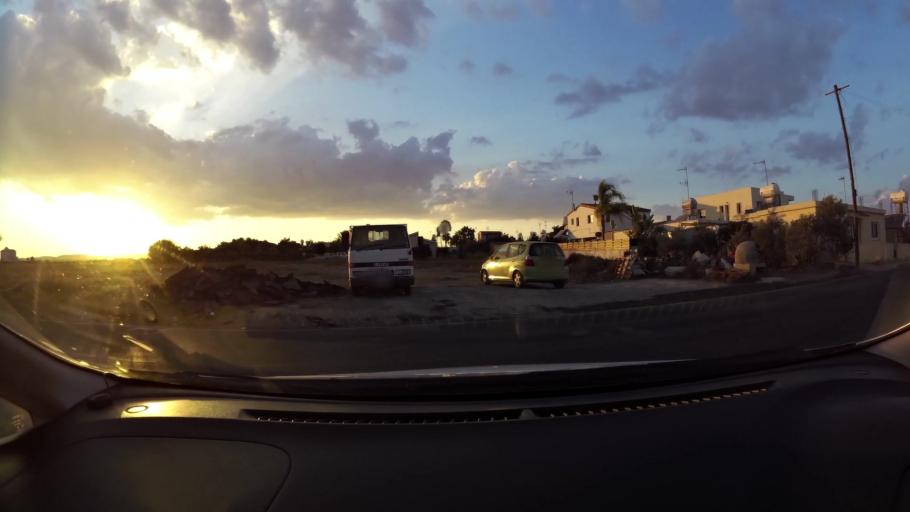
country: CY
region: Larnaka
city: Dhromolaxia
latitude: 34.8703
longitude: 33.5856
